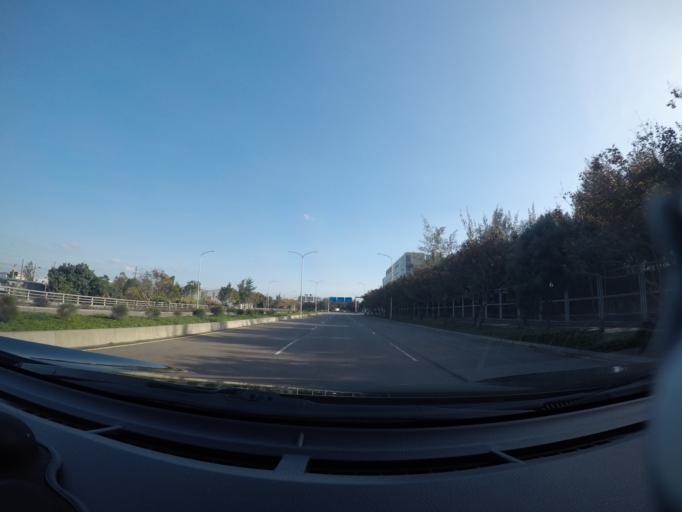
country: TW
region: Taiwan
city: Taoyuan City
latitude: 25.0968
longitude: 121.2564
